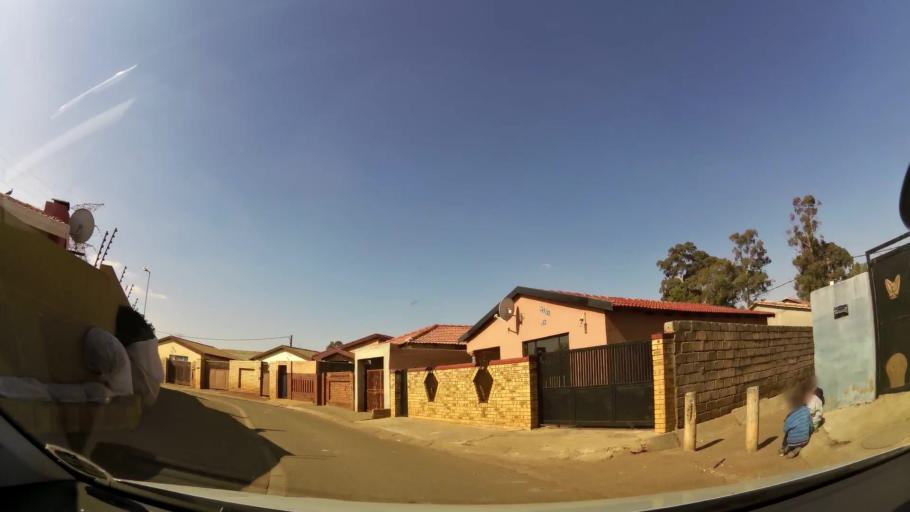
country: ZA
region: Gauteng
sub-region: City of Johannesburg Metropolitan Municipality
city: Soweto
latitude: -26.2908
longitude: 27.8570
